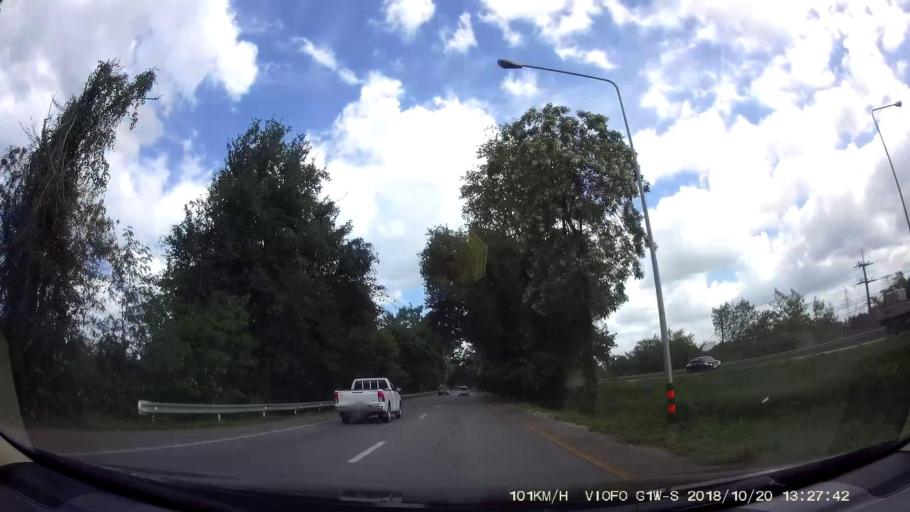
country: TH
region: Chaiyaphum
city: Khon San
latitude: 16.5923
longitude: 101.9646
